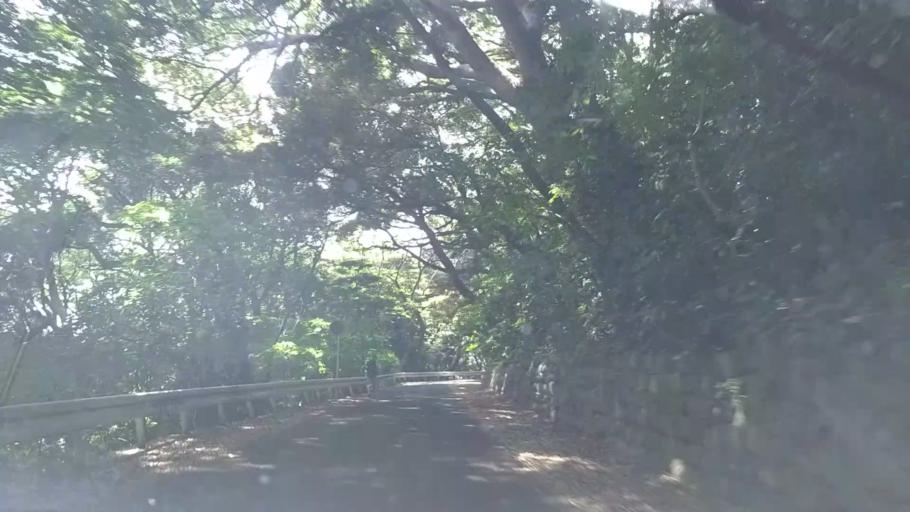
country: JP
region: Kanagawa
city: Yugawara
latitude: 35.1423
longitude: 139.1547
